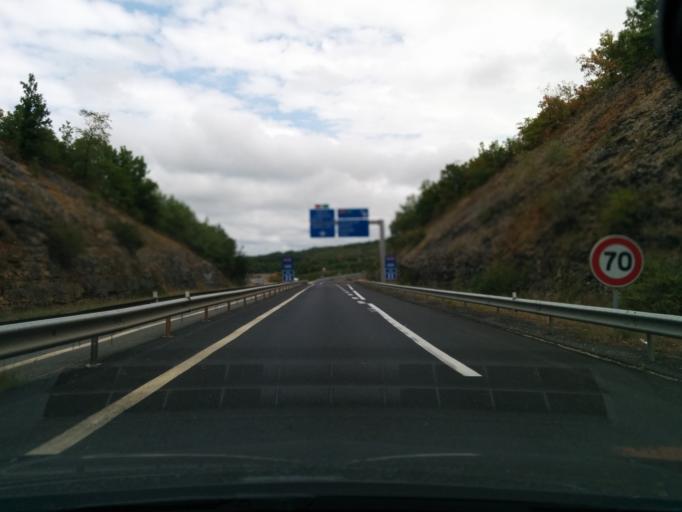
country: FR
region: Limousin
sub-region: Departement de la Correze
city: Brive-la-Gaillarde
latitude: 45.0606
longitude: 1.5019
